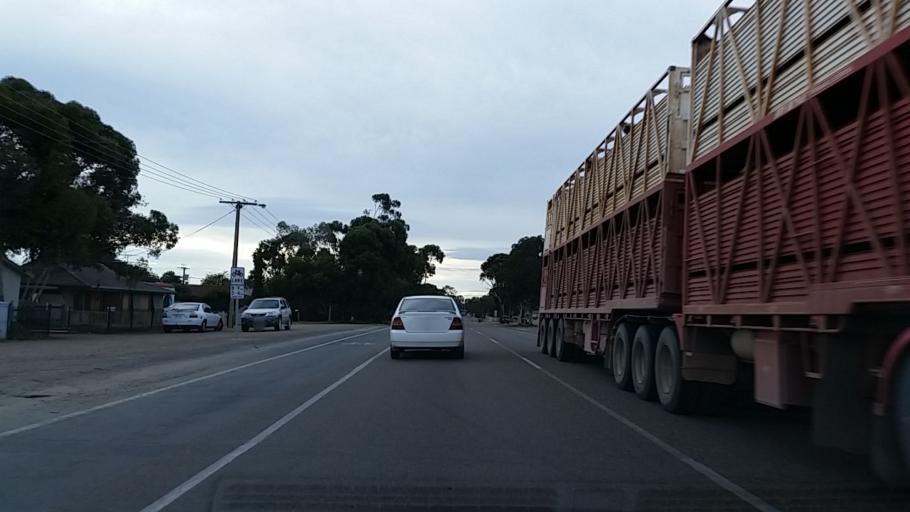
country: AU
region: South Australia
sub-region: Murray Bridge
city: Murray Bridge
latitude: -35.1426
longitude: 139.2856
